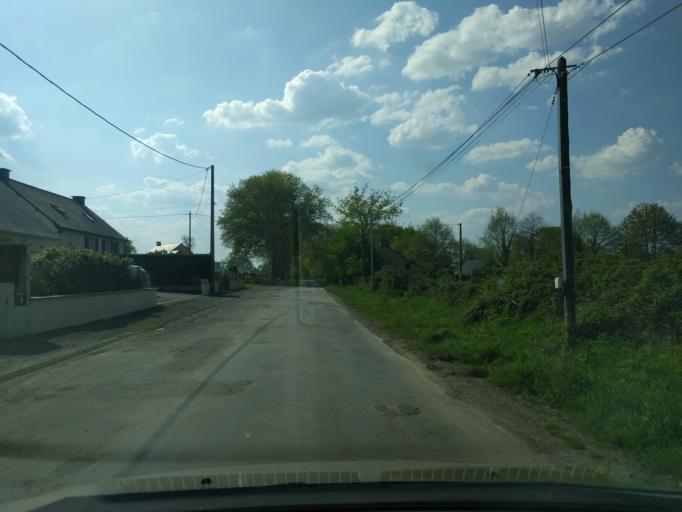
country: FR
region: Brittany
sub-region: Departement d'Ille-et-Vilaine
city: Saint-Ouen-des-Alleux
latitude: 48.2852
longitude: -1.4404
